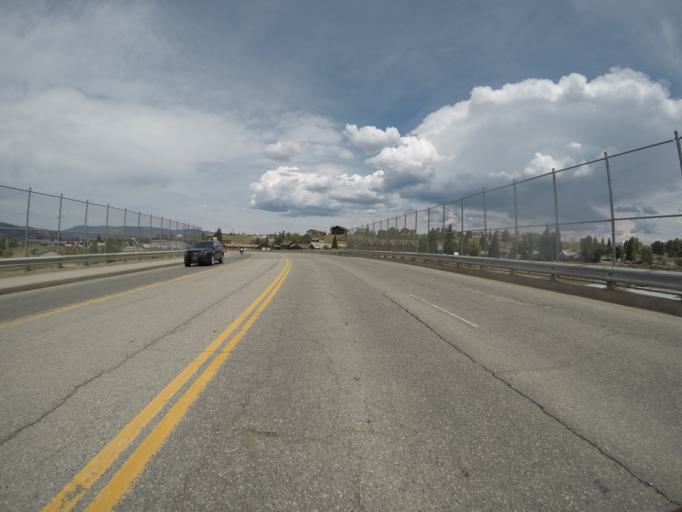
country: US
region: Colorado
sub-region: Grand County
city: Granby
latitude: 40.0835
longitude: -105.9301
